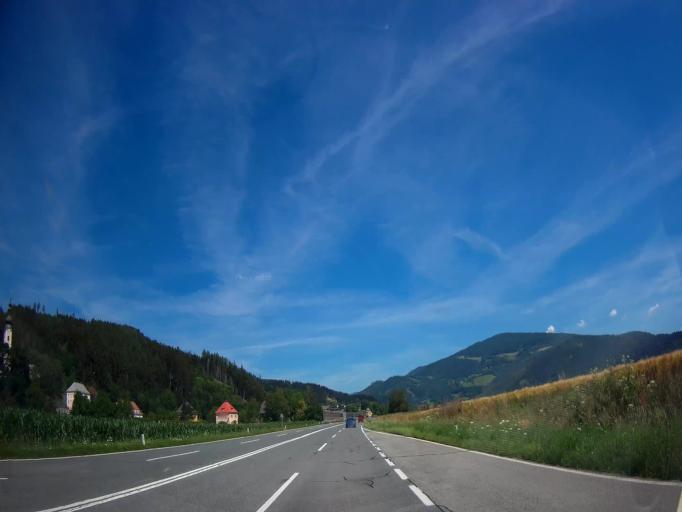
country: AT
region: Carinthia
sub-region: Politischer Bezirk Sankt Veit an der Glan
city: Molbling
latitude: 46.8656
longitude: 14.4492
